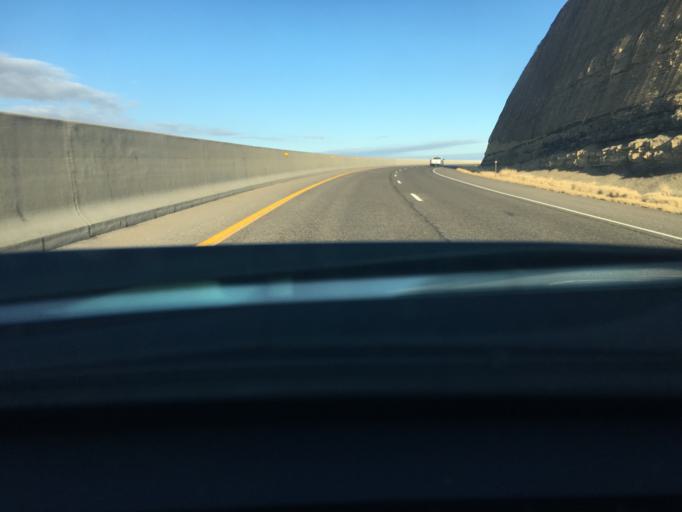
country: US
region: Colorado
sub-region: Delta County
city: Delta
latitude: 38.8121
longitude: -108.2939
